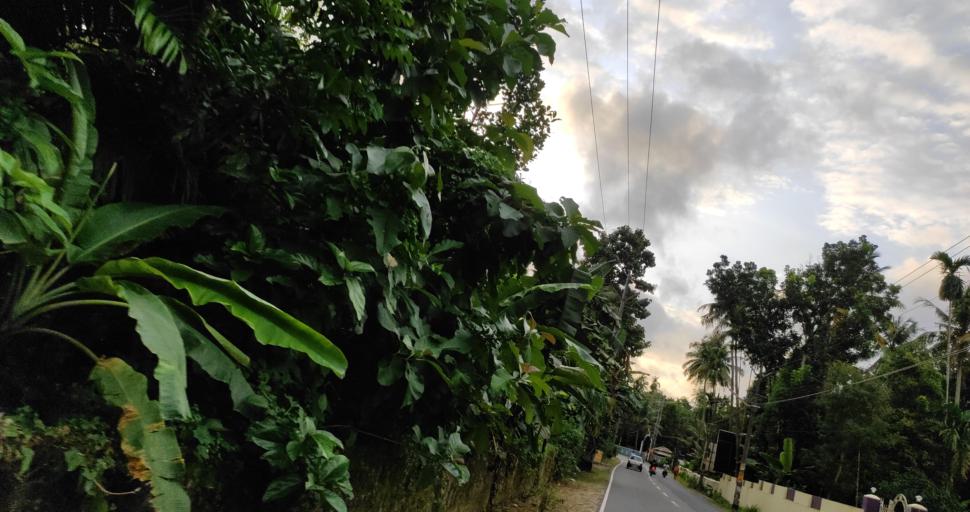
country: IN
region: Kerala
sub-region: Thrissur District
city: Kizhake Chalakudi
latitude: 10.3177
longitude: 76.3847
